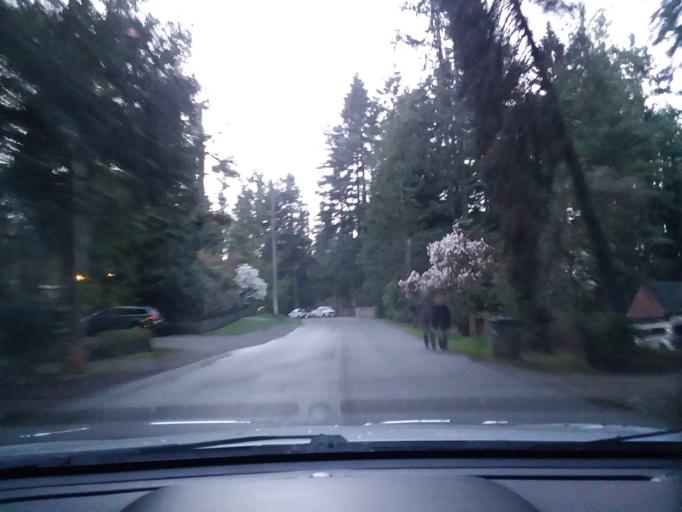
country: US
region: Washington
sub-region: King County
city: Lake Forest Park
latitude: 47.7601
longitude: -122.2921
